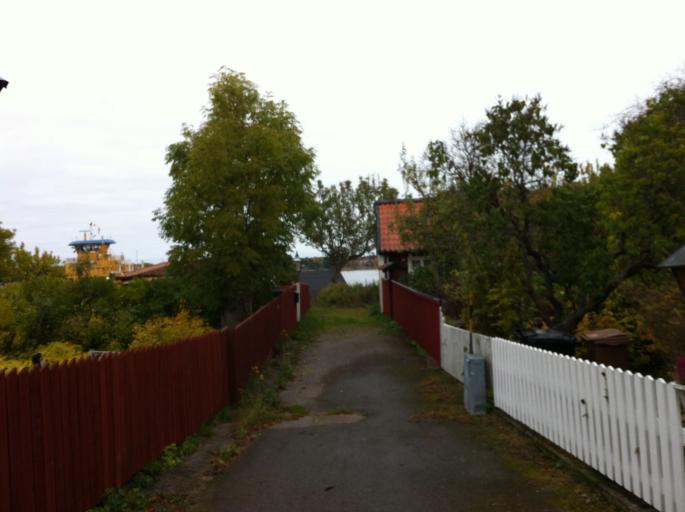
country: SE
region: Uppsala
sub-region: Osthammars Kommun
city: Oregrund
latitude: 60.3398
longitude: 18.4468
